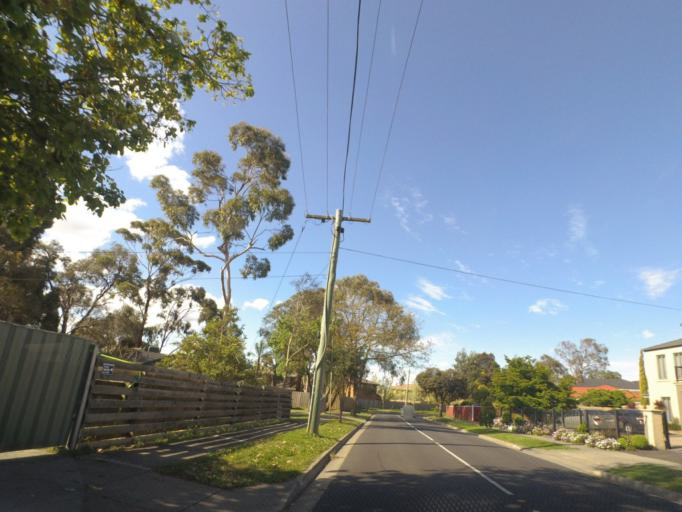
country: AU
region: Victoria
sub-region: Knox
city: Knoxfield
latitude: -37.8842
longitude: 145.2486
